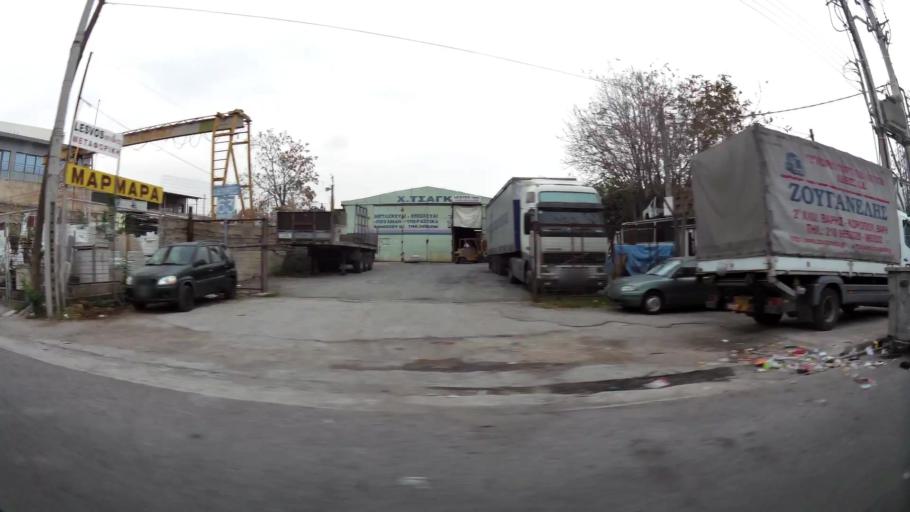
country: GR
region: Attica
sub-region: Nomarchia Athinas
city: Aigaleo
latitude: 37.9883
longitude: 23.6859
